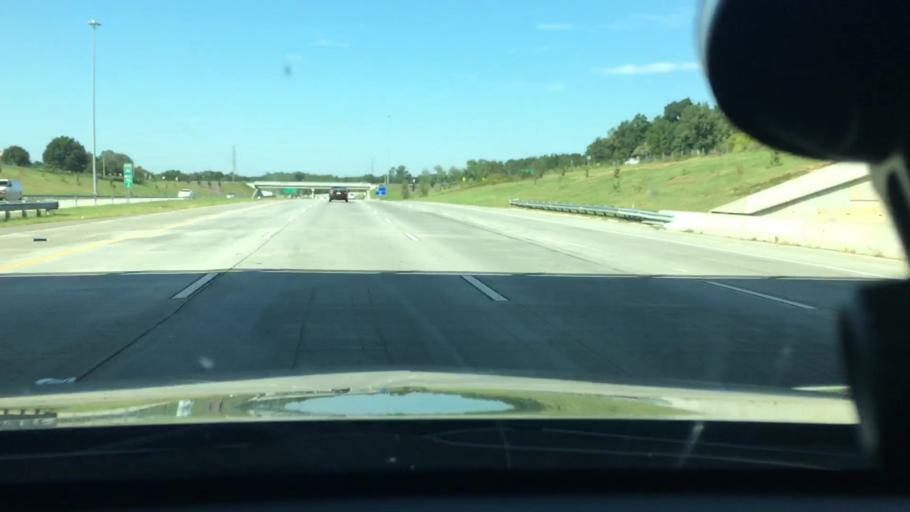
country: US
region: North Carolina
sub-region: Mecklenburg County
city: Huntersville
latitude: 35.3690
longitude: -80.7846
